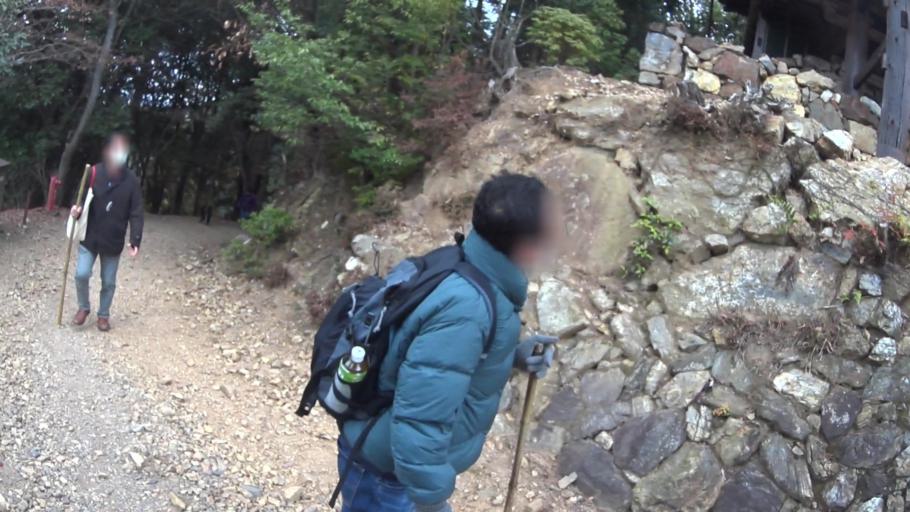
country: JP
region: Kyoto
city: Uji
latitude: 34.9438
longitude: 135.8399
